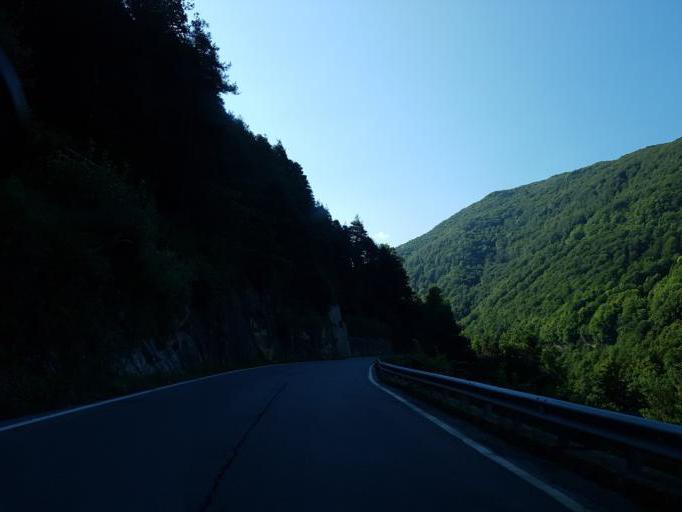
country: IT
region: Piedmont
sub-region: Provincia di Cuneo
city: San Damiano Macra
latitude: 44.4922
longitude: 7.2427
